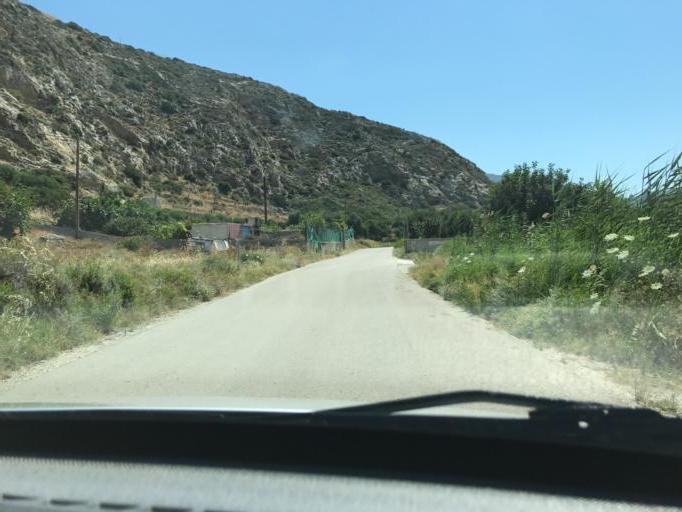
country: GR
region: South Aegean
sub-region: Nomos Dodekanisou
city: Karpathos
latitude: 35.5021
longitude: 27.1998
